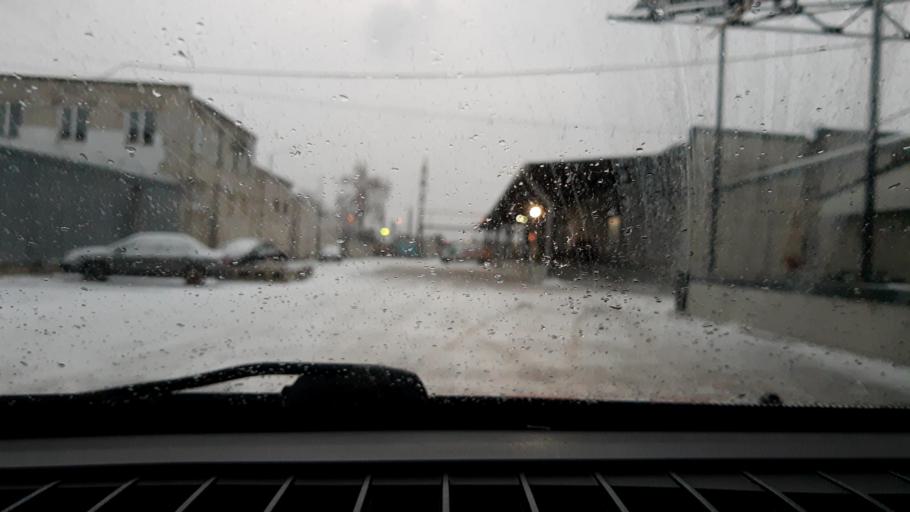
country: RU
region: Nizjnij Novgorod
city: Nizhniy Novgorod
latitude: 56.2960
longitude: 43.8862
